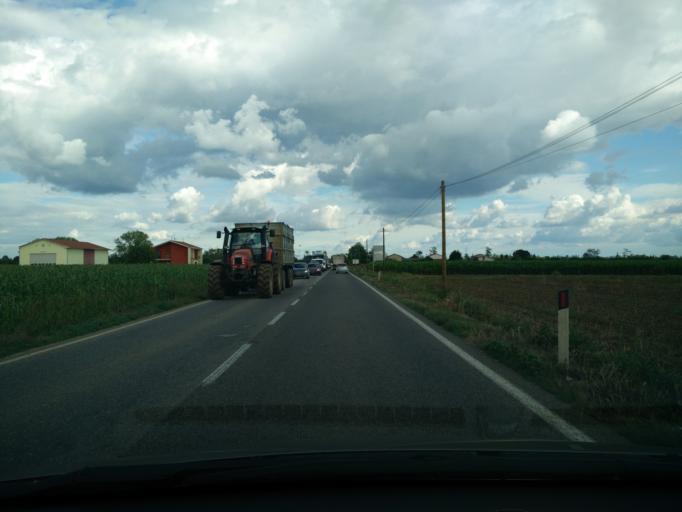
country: IT
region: Veneto
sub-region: Provincia di Treviso
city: Fossalunga
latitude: 45.7082
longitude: 12.0669
